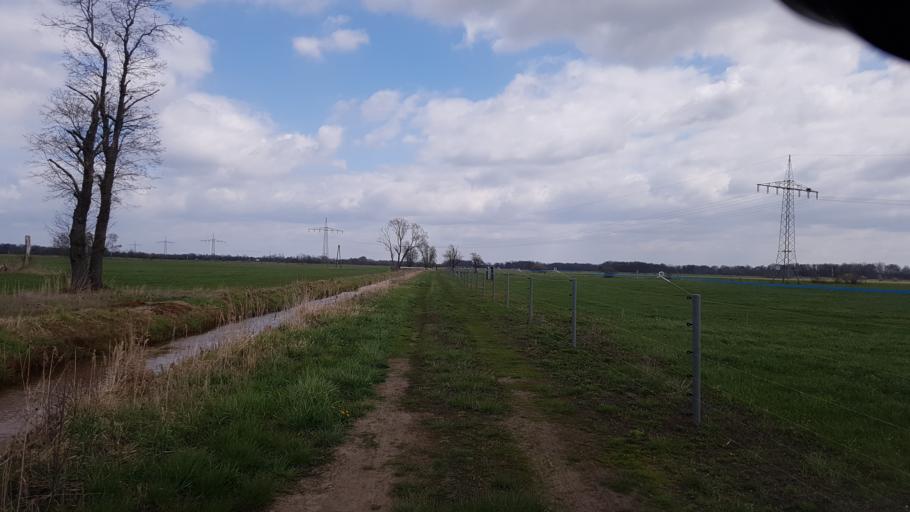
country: DE
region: Brandenburg
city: Schraden
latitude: 51.4663
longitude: 13.6855
